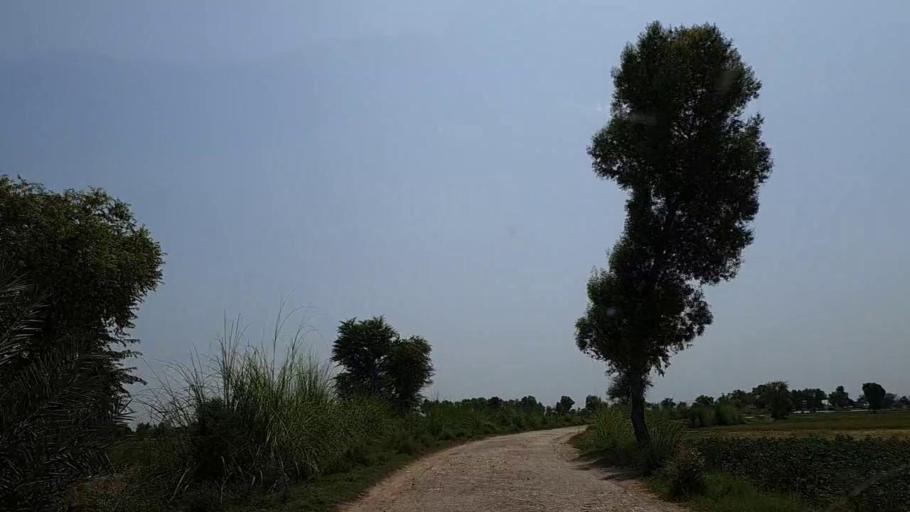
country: PK
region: Sindh
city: Adilpur
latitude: 27.9022
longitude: 69.3607
